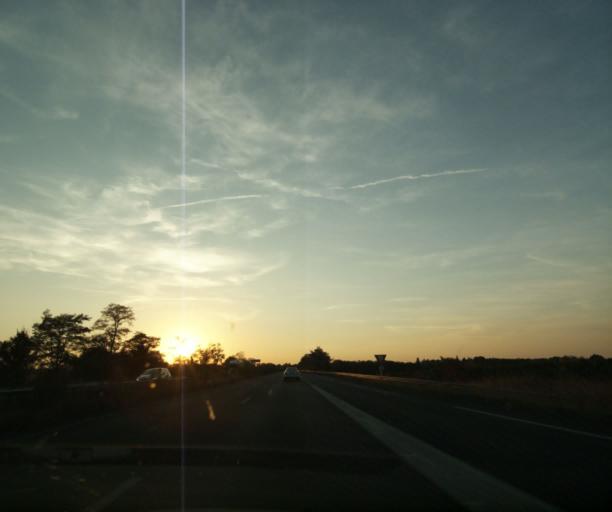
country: FR
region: Aquitaine
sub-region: Departement du Lot-et-Garonne
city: Meilhan-sur-Garonne
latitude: 44.4757
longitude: 0.0355
